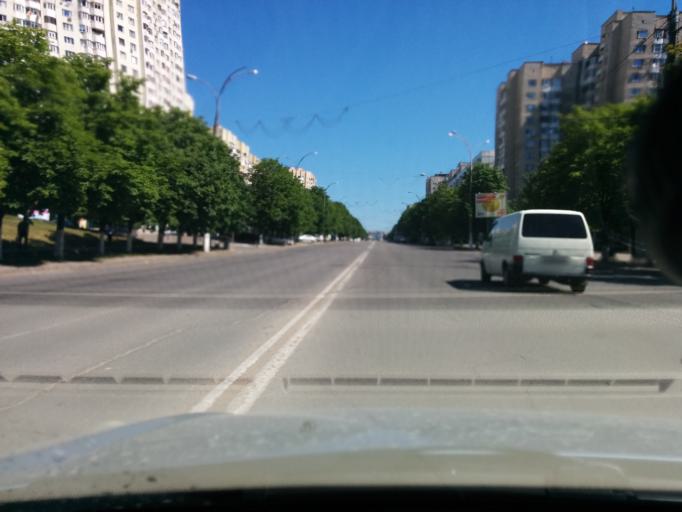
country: MD
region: Chisinau
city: Chisinau
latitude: 47.0499
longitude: 28.8635
